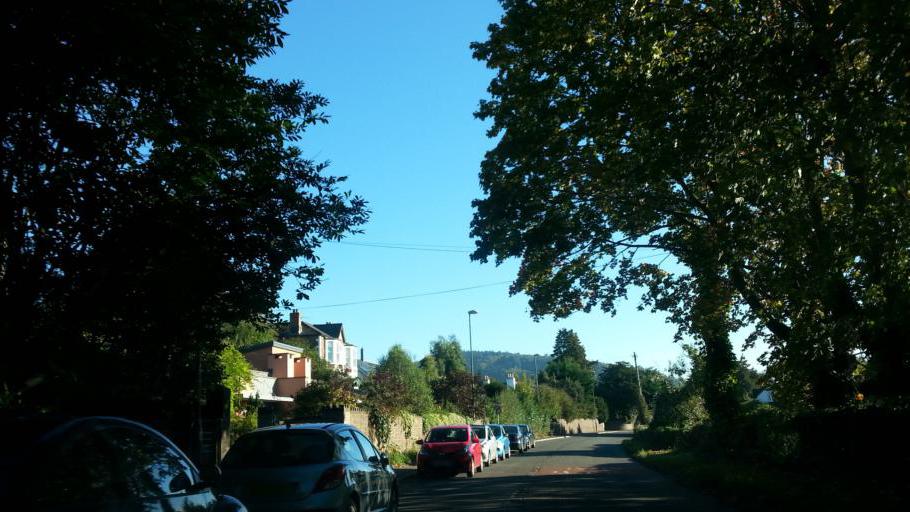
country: GB
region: Wales
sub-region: Monmouthshire
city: Monmouth
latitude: 51.8165
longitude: -2.7083
